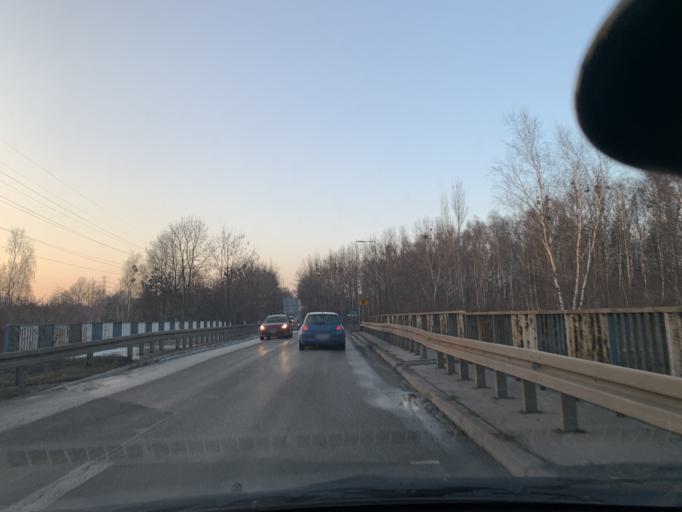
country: PL
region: Silesian Voivodeship
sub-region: Piekary Slaskie
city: Piekary Slaskie
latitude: 50.3712
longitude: 18.9163
